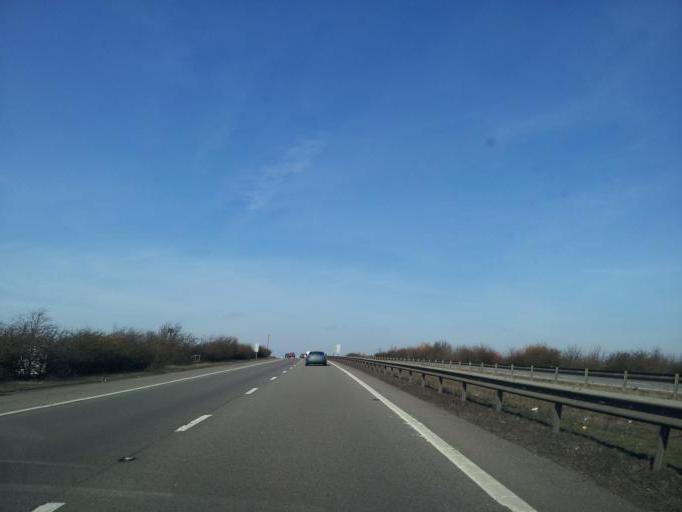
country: GB
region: England
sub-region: Cambridgeshire
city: Brampton
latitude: 52.3295
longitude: -0.2478
